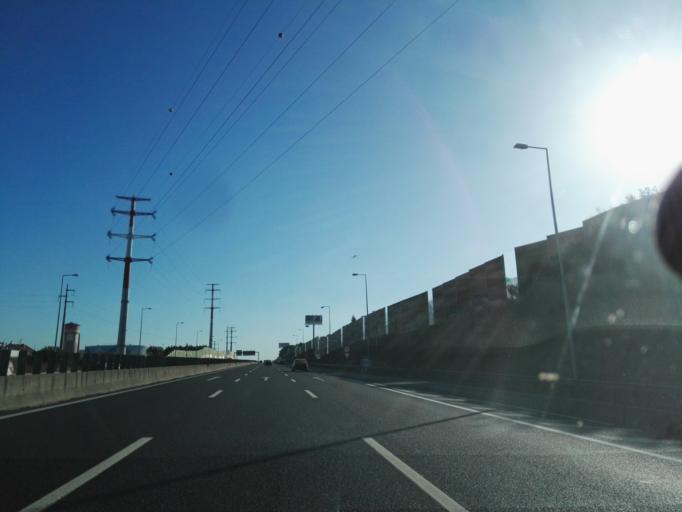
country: PT
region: Lisbon
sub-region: Loures
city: Santa Iria da Azoia
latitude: 38.8474
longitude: -9.0900
